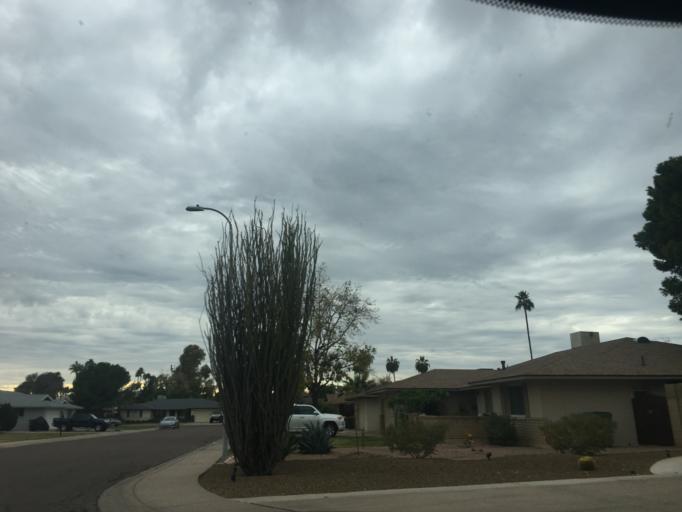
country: US
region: Arizona
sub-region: Maricopa County
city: Guadalupe
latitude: 33.3683
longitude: -111.9249
